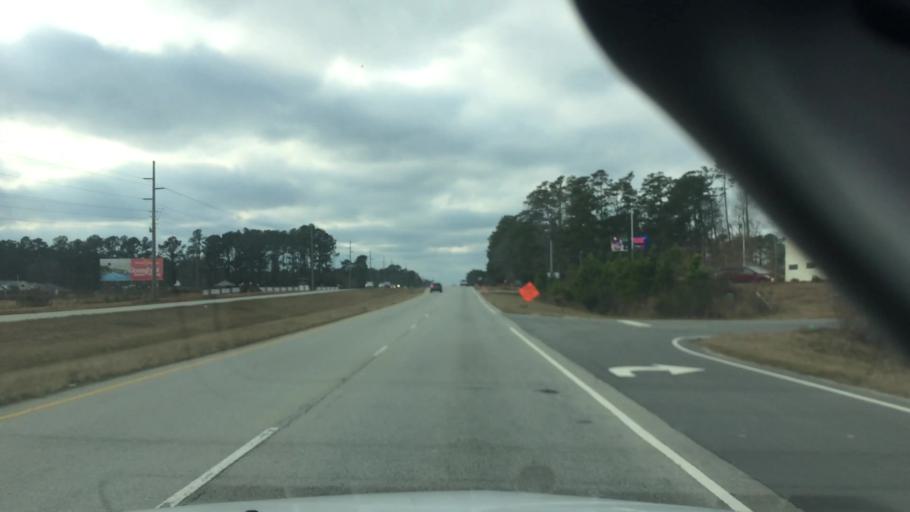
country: US
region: North Carolina
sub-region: Brunswick County
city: Shallotte
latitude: 33.9570
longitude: -78.4336
